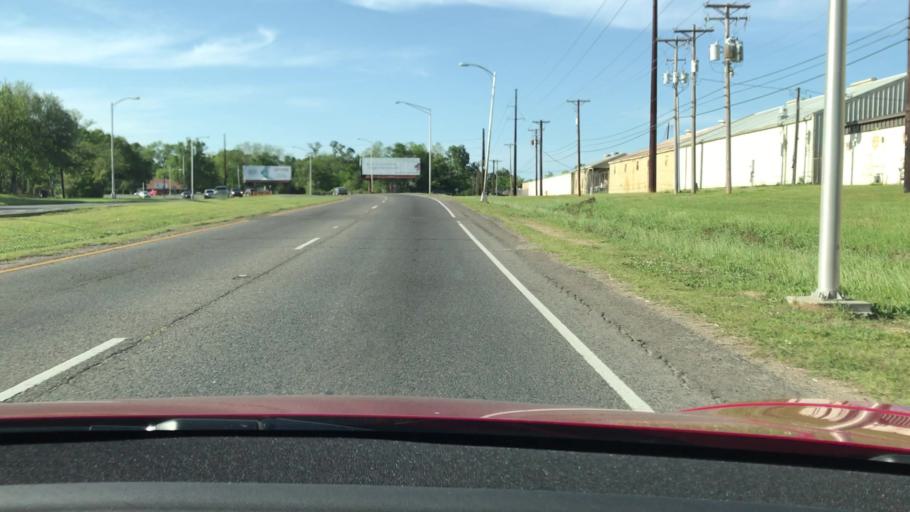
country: US
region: Louisiana
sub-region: Bossier Parish
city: Bossier City
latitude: 32.5008
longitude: -93.7248
